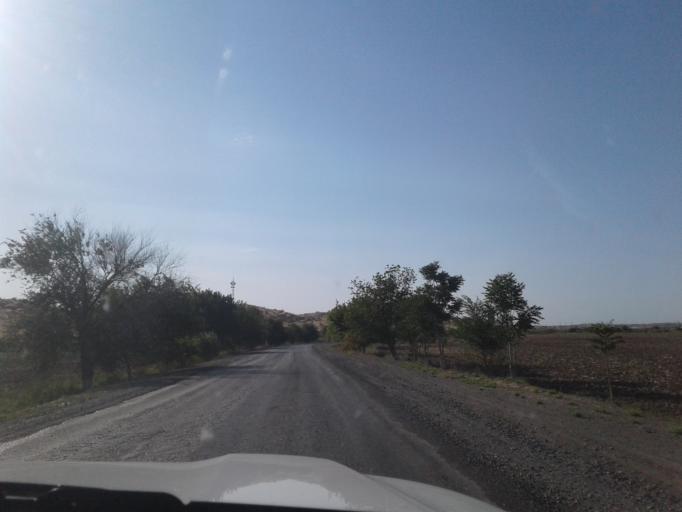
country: TM
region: Mary
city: Yoloeten
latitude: 36.9494
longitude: 62.4618
